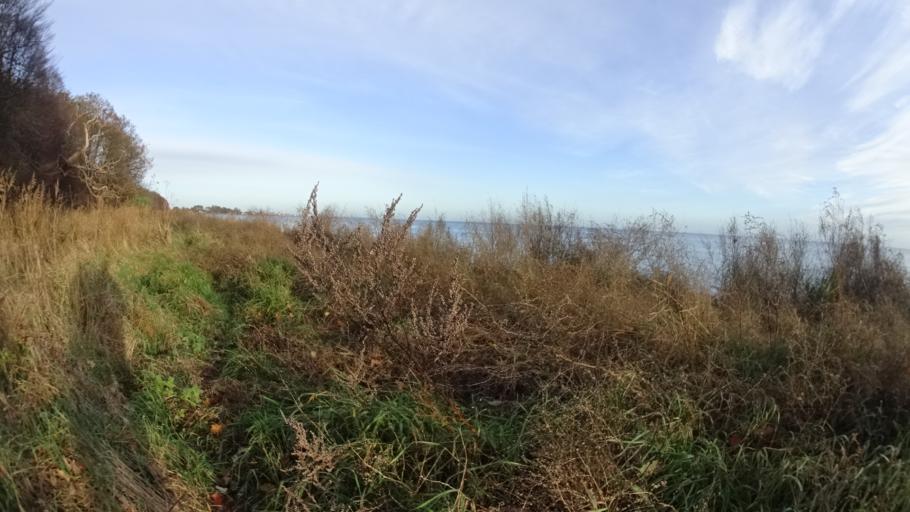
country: DK
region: Central Jutland
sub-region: Odder Kommune
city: Odder
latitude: 55.9065
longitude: 10.2357
